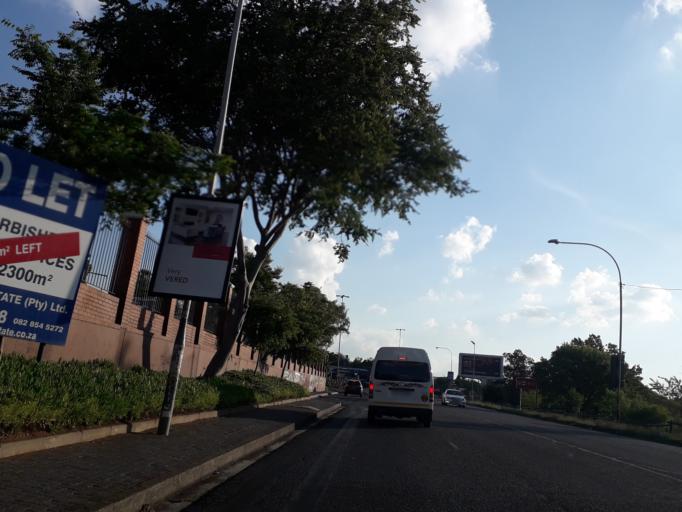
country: ZA
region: Gauteng
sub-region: City of Johannesburg Metropolitan Municipality
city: Johannesburg
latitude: -26.1421
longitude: 28.0086
